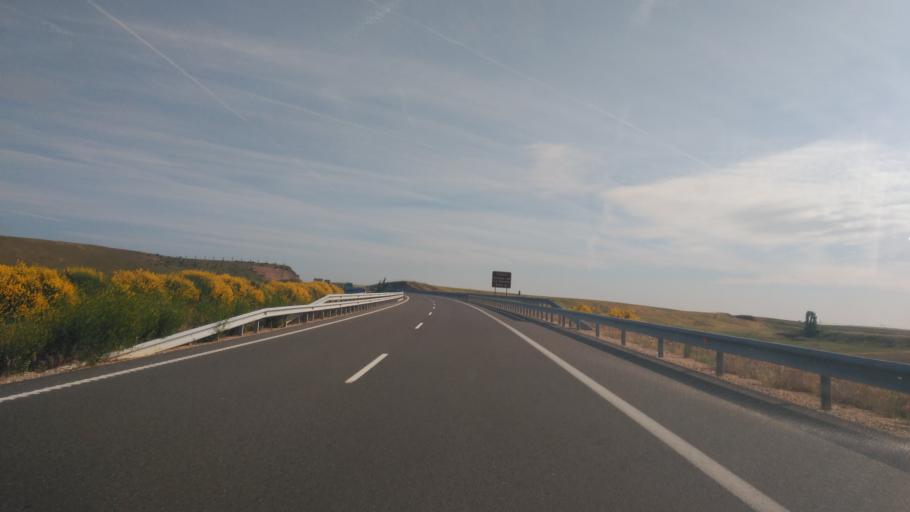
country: ES
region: Castille and Leon
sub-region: Provincia de Salamanca
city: Monterrubio de Armuna
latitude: 41.0382
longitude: -5.6678
